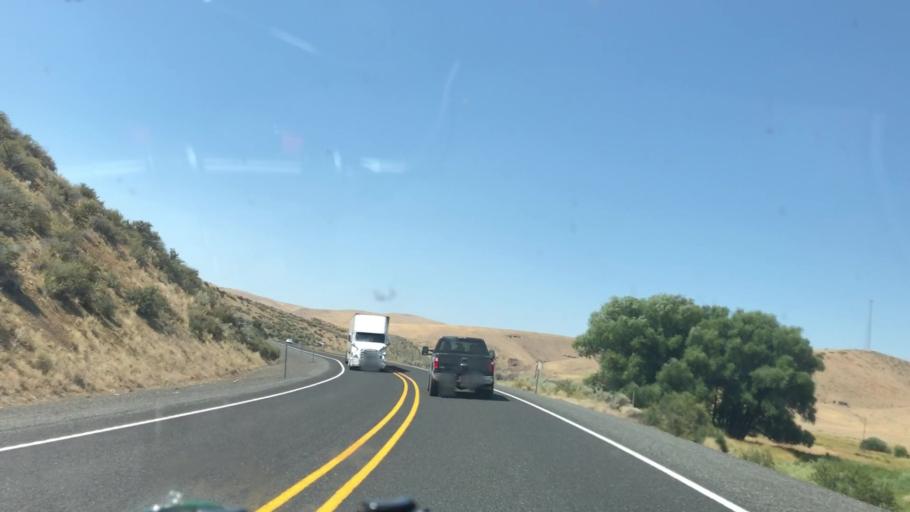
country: US
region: Idaho
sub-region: Owyhee County
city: Marsing
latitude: 43.2234
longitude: -117.0511
